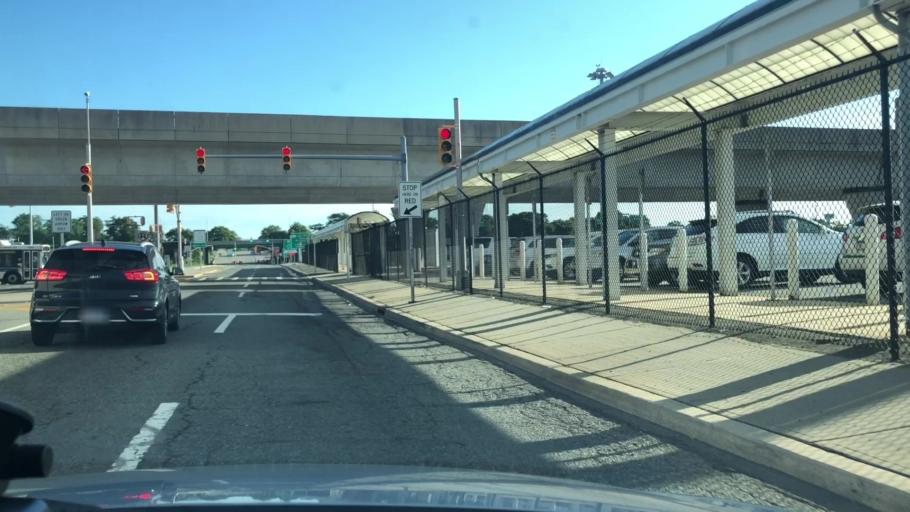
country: US
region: New York
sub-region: Queens County
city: Borough of Queens
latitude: 40.6612
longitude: -73.8237
